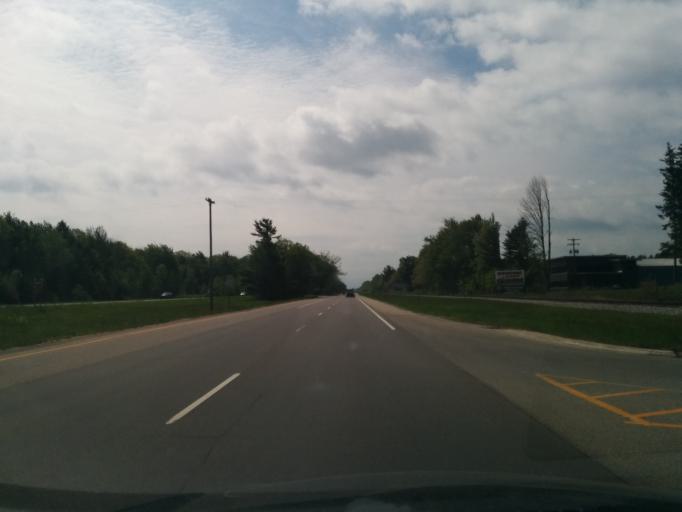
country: US
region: Michigan
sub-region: Ottawa County
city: Grand Haven
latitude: 43.0013
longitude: -86.2015
